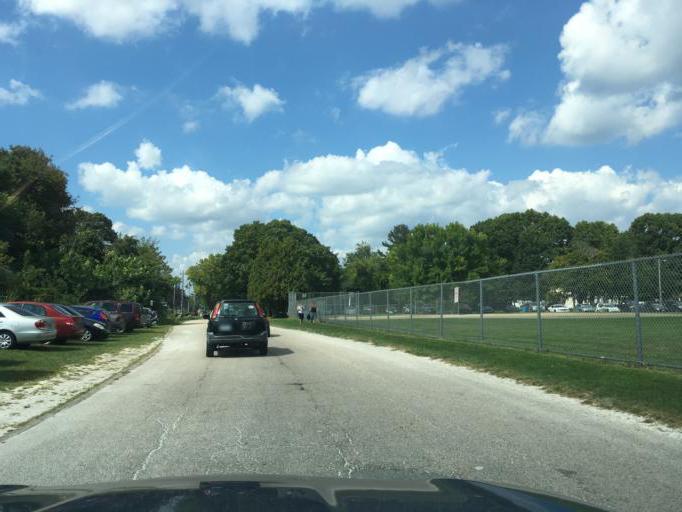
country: US
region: Rhode Island
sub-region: Kent County
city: Warwick
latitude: 41.6849
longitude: -71.3970
